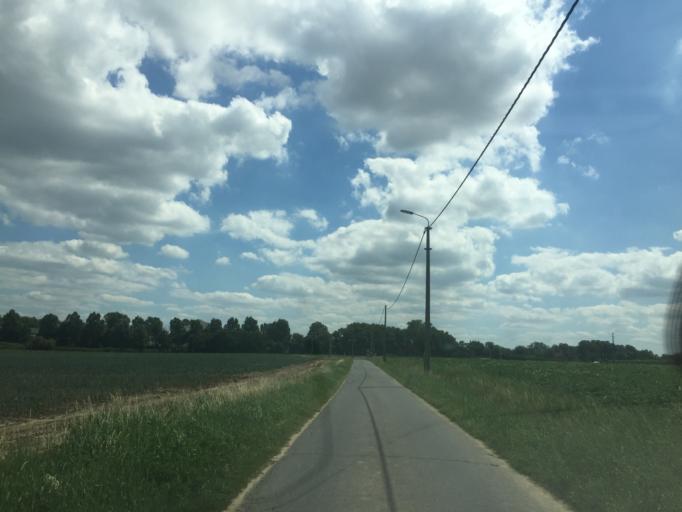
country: BE
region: Flanders
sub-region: Provincie West-Vlaanderen
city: Staden
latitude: 50.9674
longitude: 2.9945
